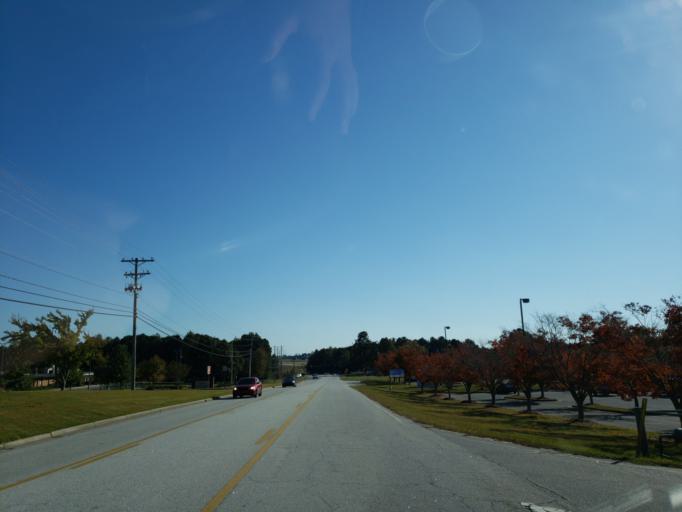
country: US
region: Georgia
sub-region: Gwinnett County
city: Lawrenceville
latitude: 33.9852
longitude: -83.9727
